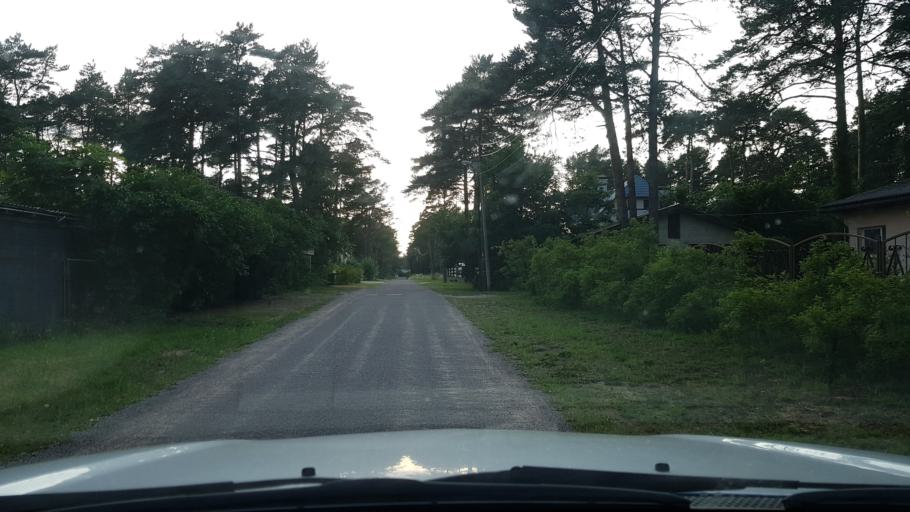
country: EE
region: Ida-Virumaa
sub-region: Narva-Joesuu linn
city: Narva-Joesuu
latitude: 59.4542
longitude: 28.0570
